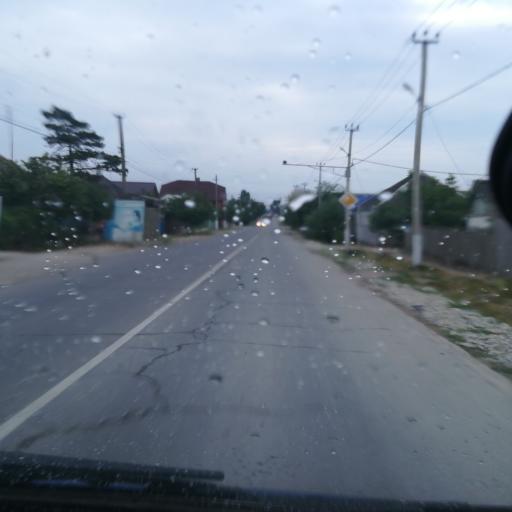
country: RU
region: Krasnodarskiy
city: Krymsk
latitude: 44.9367
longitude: 37.9745
